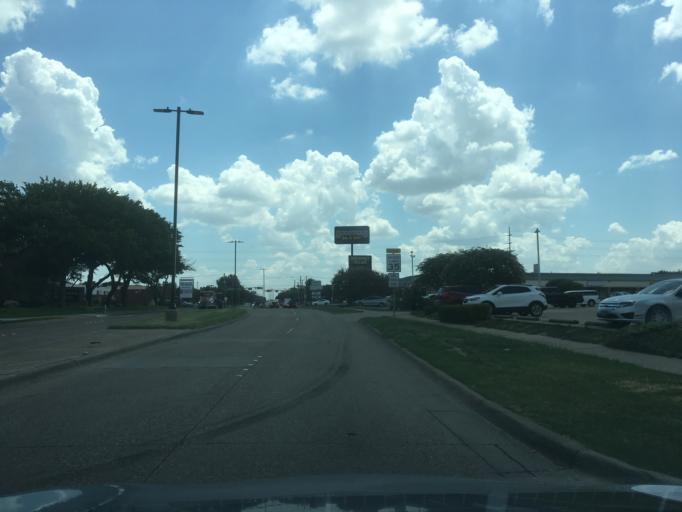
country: US
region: Texas
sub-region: Dallas County
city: Garland
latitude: 32.8661
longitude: -96.6484
